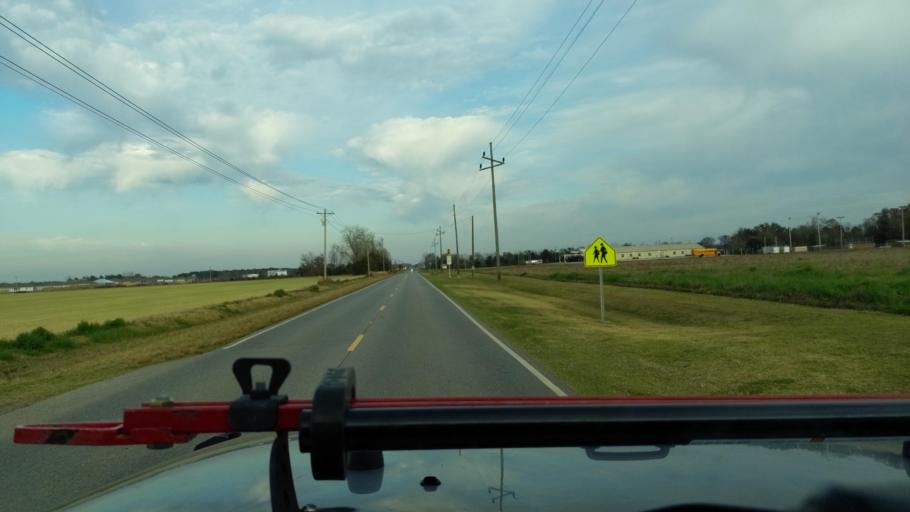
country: US
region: Alabama
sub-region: Baldwin County
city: Foley
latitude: 30.4579
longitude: -87.7044
